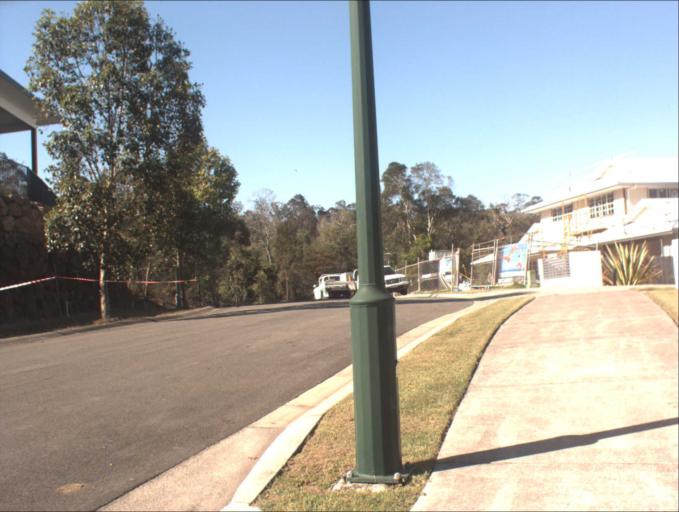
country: AU
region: Queensland
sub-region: Logan
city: Slacks Creek
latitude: -27.6297
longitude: 153.1578
